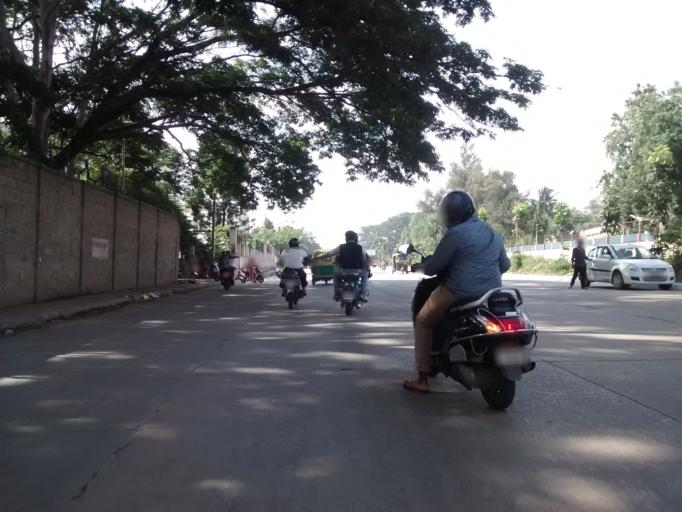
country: IN
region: Karnataka
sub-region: Bangalore Urban
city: Bangalore
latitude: 12.9816
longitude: 77.6505
